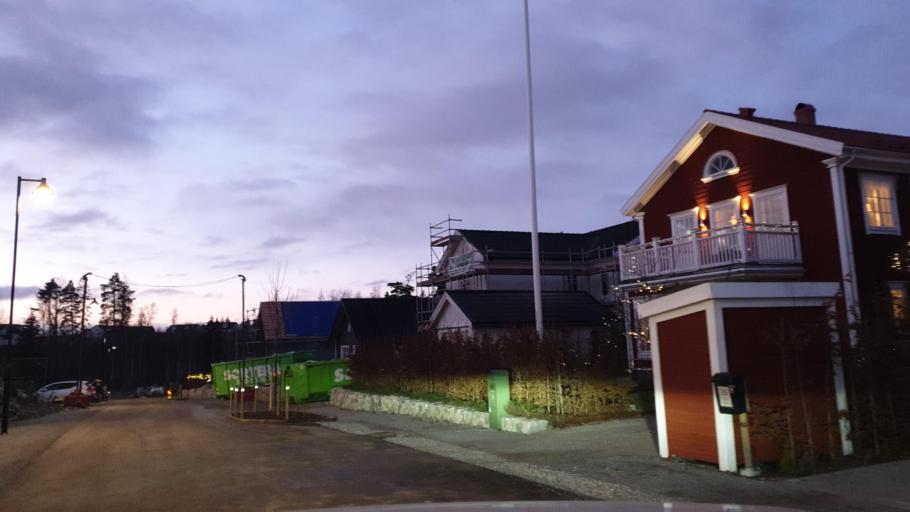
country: SE
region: Stockholm
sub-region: Sigtuna Kommun
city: Marsta
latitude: 59.6074
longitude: 17.8045
